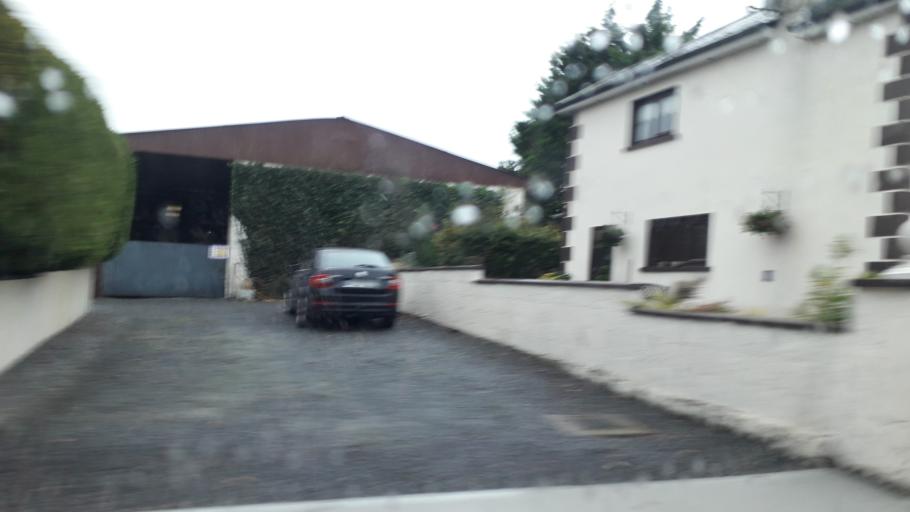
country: IE
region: Connaught
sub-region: Roscommon
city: Roscommon
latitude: 53.7768
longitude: -8.2475
